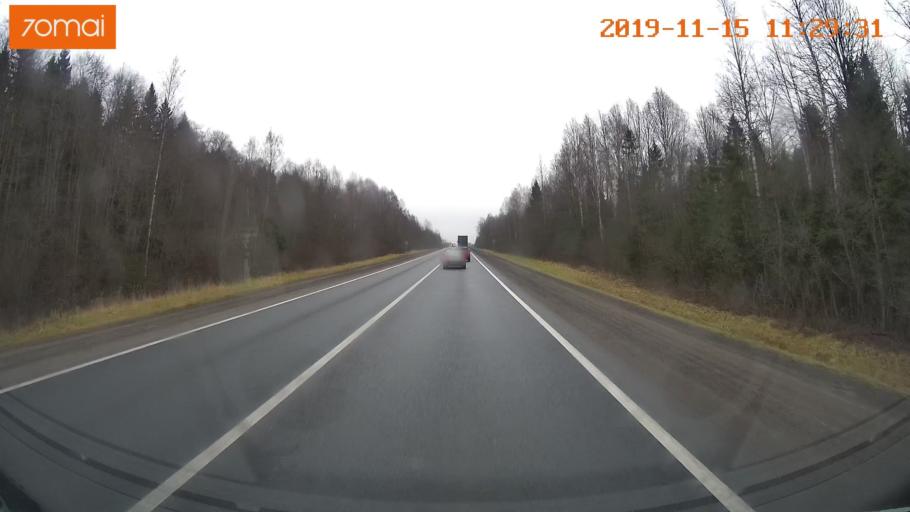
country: RU
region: Vologda
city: Molochnoye
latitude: 59.1753
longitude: 39.5110
